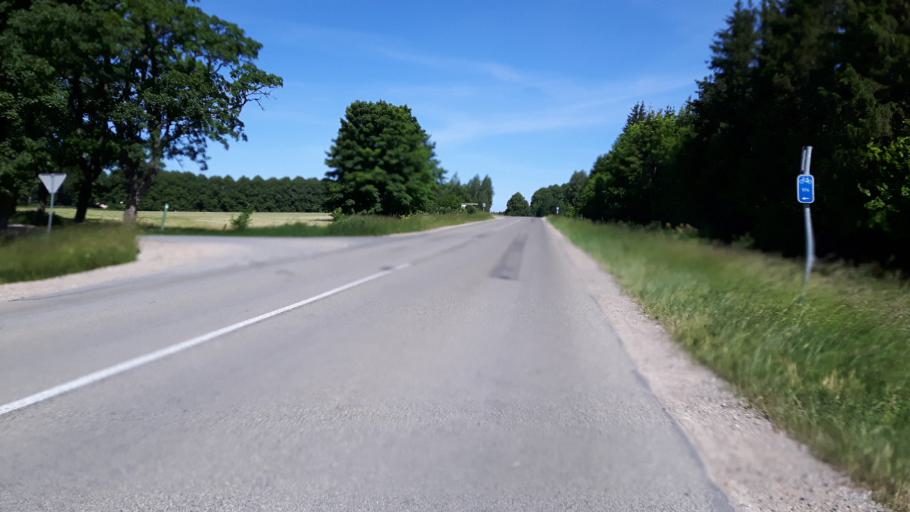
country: LV
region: Tukuma Rajons
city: Tukums
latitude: 56.9970
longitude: 23.0864
